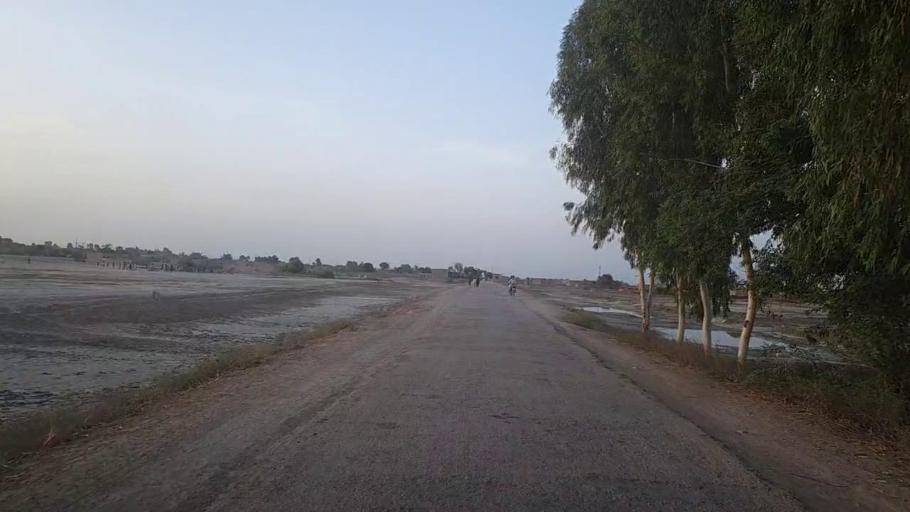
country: PK
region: Sindh
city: Radhan
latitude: 27.1300
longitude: 67.9301
